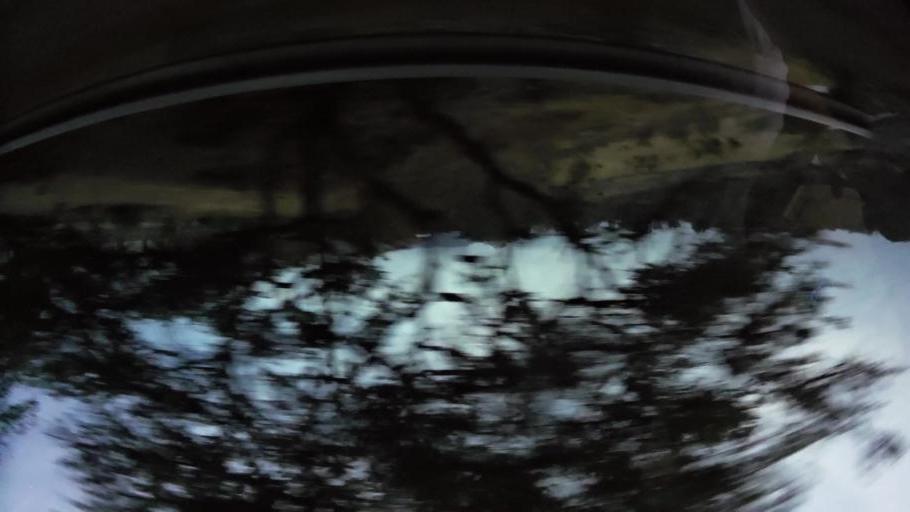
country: NI
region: Esteli
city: Esteli
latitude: 13.1060
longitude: -86.3560
